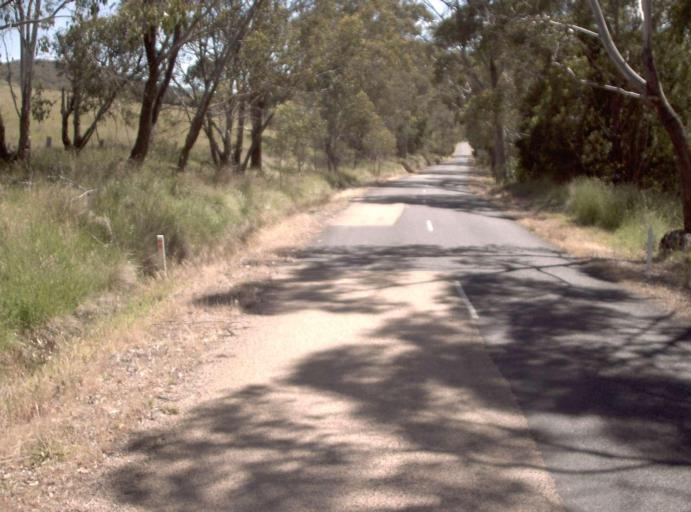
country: AU
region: New South Wales
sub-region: Bombala
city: Bombala
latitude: -37.0518
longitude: 148.8074
